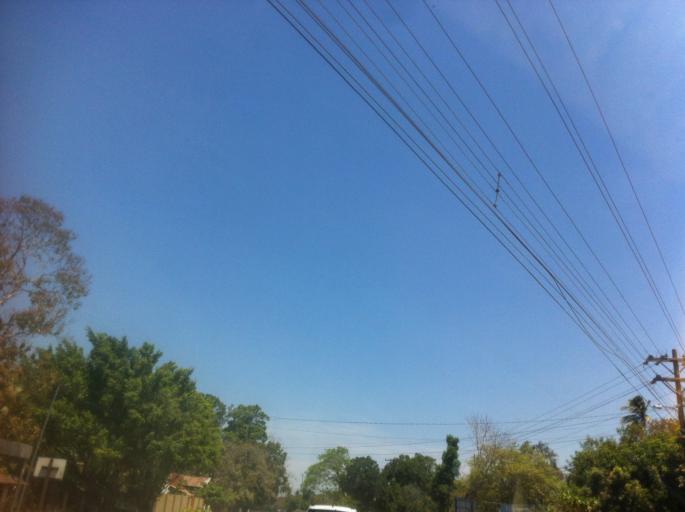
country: CR
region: Guanacaste
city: Belen
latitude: 10.4507
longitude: -85.5550
